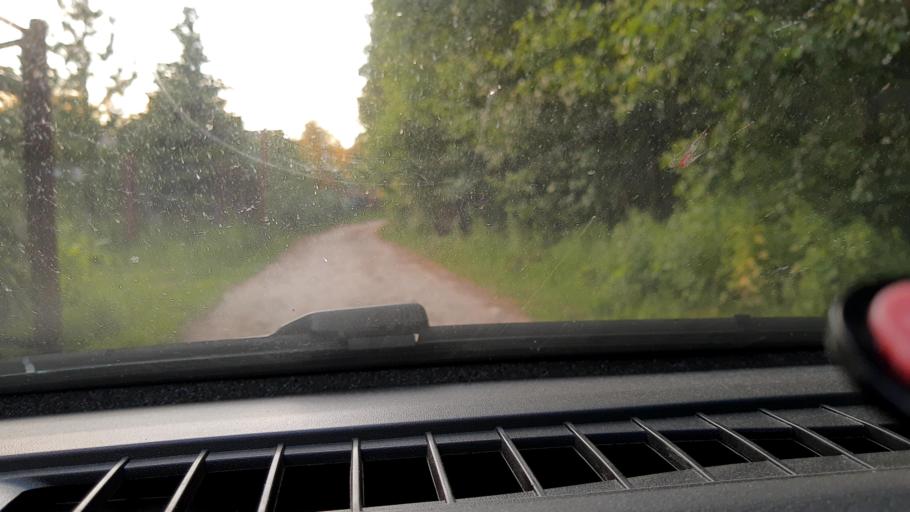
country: RU
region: Nizjnij Novgorod
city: Afonino
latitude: 56.3163
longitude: 44.2029
